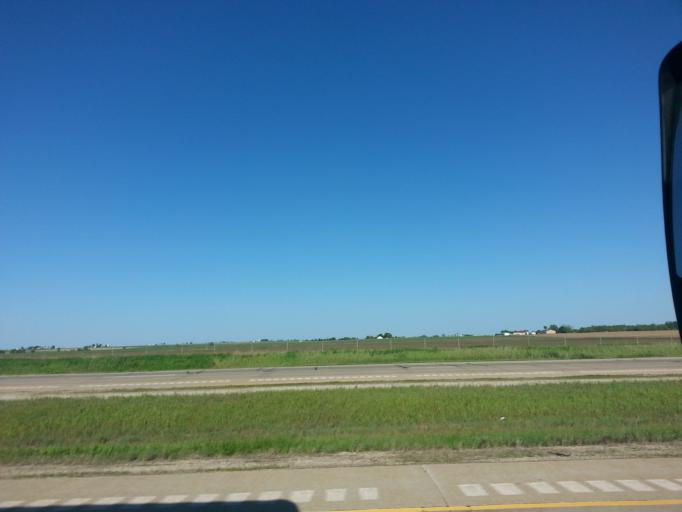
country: US
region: Illinois
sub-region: Marshall County
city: Wenona
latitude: 41.0667
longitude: -89.0673
